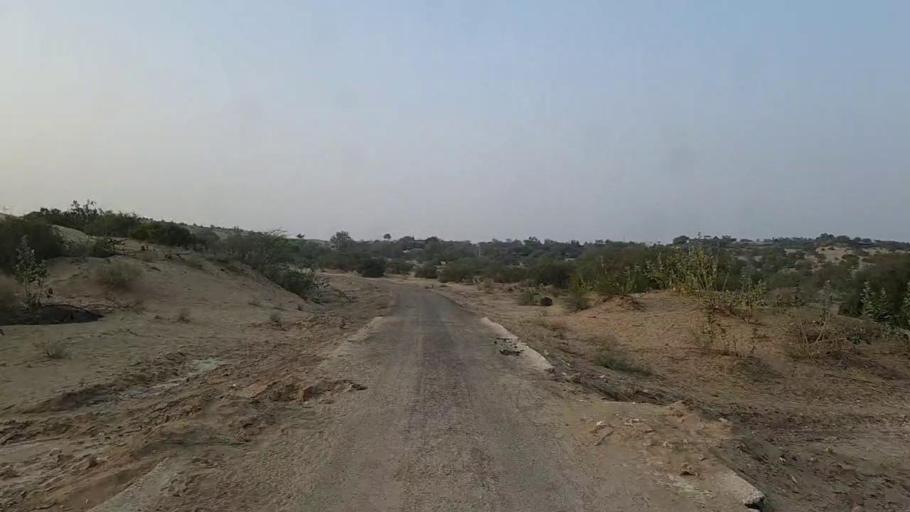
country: PK
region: Sindh
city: Naukot
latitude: 24.6800
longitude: 69.4587
